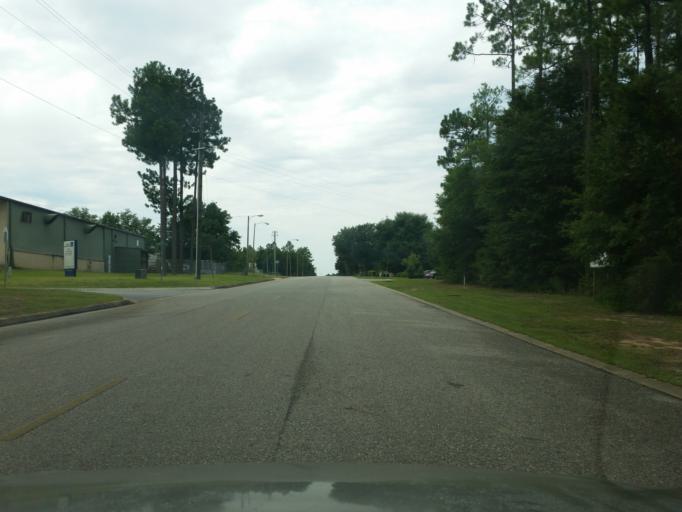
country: US
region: Florida
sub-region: Santa Rosa County
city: East Milton
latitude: 30.6420
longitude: -86.9841
